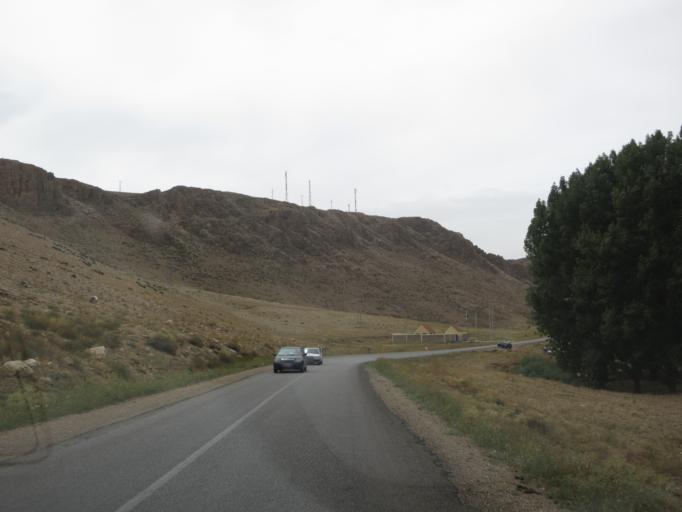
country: MA
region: Meknes-Tafilalet
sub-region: Khenifra
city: Itzer
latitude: 33.1610
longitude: -5.0660
